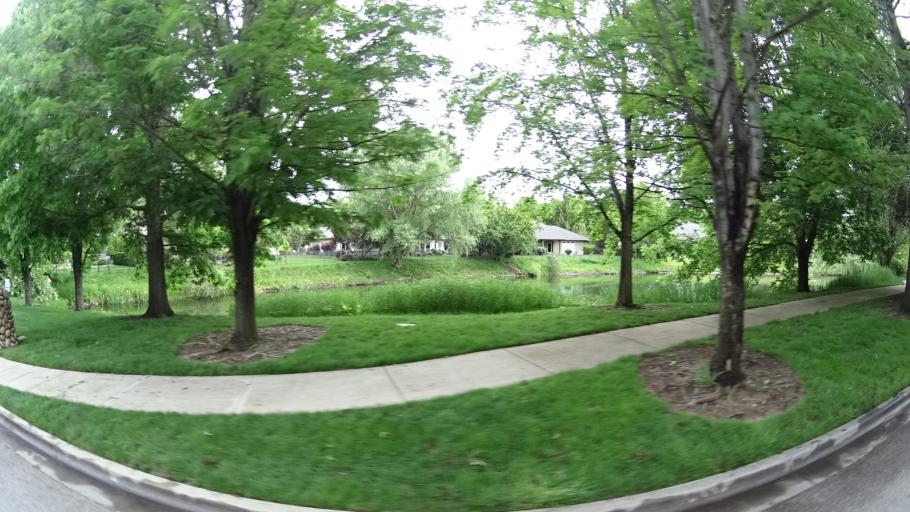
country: US
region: Idaho
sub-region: Ada County
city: Eagle
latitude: 43.6797
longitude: -116.3464
